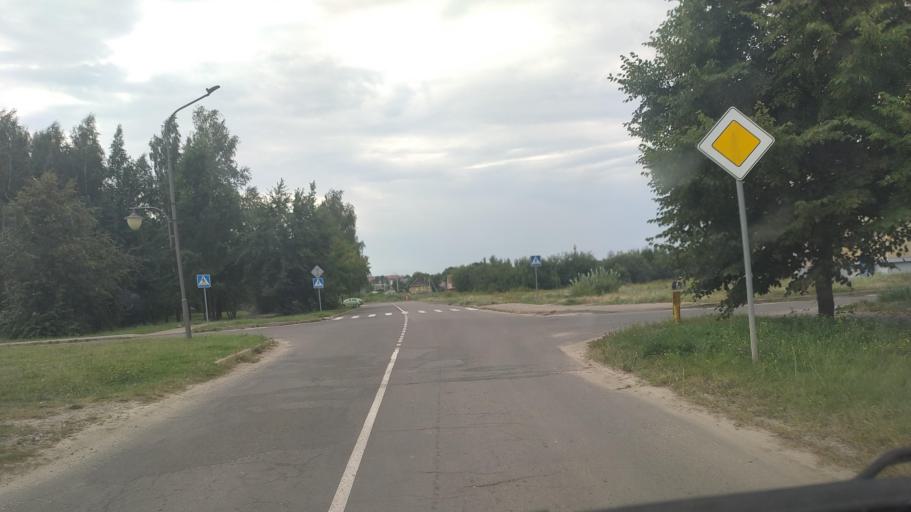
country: BY
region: Brest
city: Byaroza
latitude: 52.5391
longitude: 24.9719
